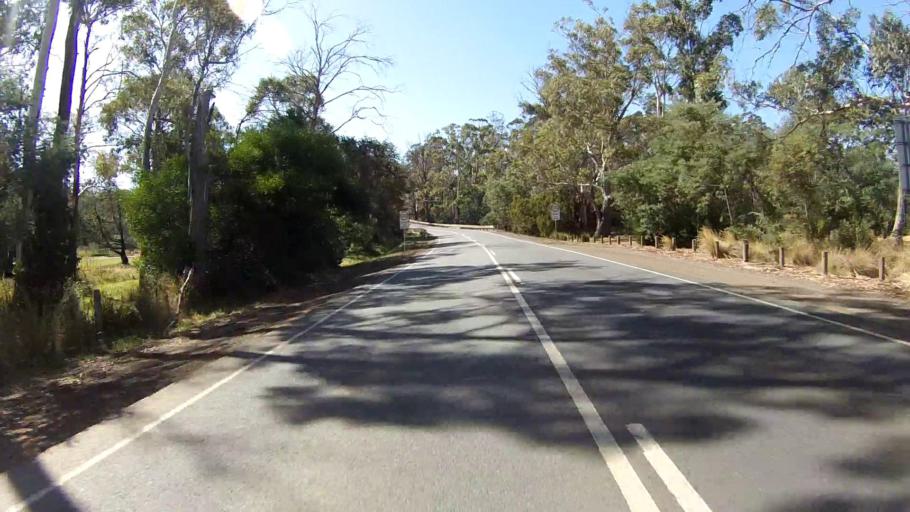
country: AU
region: Tasmania
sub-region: Sorell
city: Sorell
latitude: -42.5463
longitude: 147.8863
